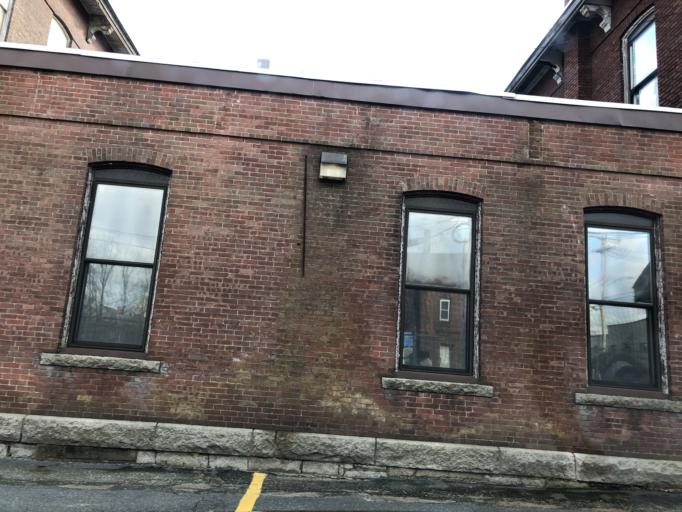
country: US
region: Massachusetts
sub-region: Bristol County
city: New Bedford
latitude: 41.6528
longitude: -70.9245
